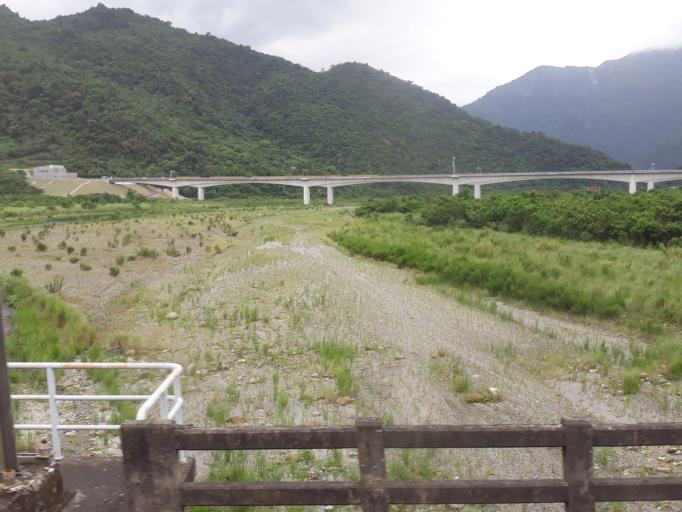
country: TW
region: Taiwan
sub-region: Yilan
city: Yilan
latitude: 24.4417
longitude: 121.7796
